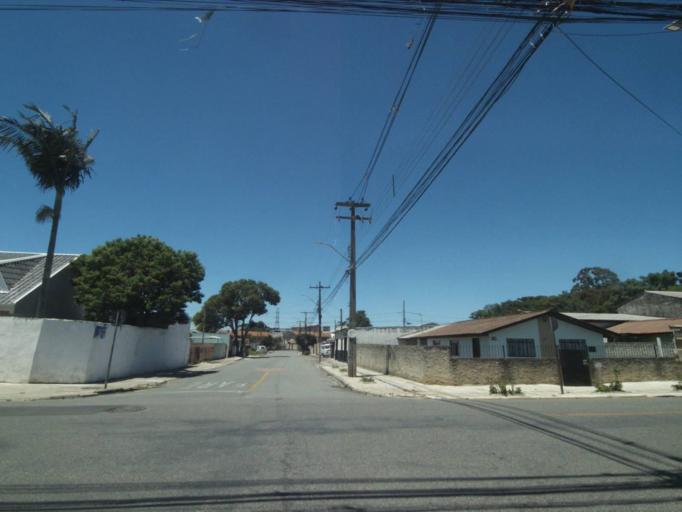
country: BR
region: Parana
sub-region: Curitiba
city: Curitiba
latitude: -25.4755
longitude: -49.3455
